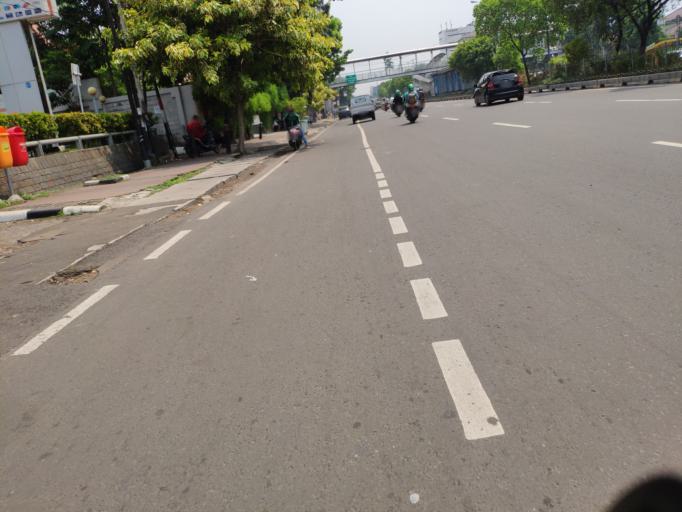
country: ID
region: Jakarta Raya
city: Jakarta
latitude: -6.2077
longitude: 106.8591
